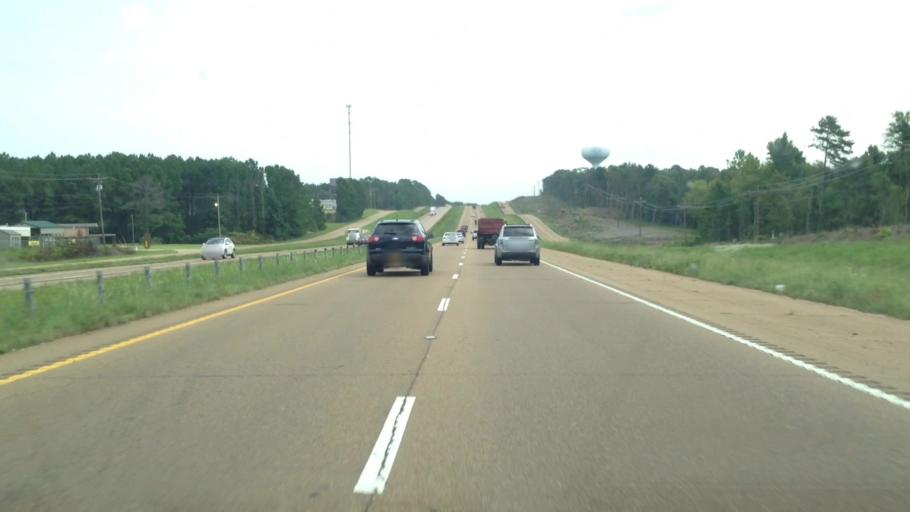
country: US
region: Mississippi
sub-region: Hinds County
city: Byram
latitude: 32.1511
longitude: -90.2772
